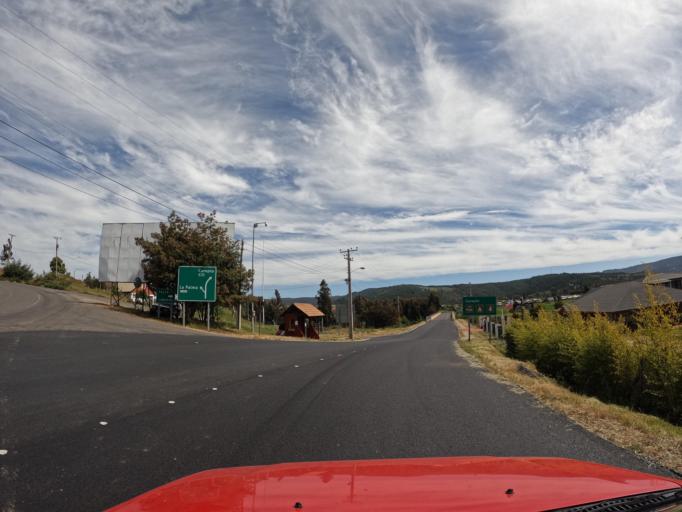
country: CL
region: Maule
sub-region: Provincia de Talca
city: Constitucion
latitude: -35.0849
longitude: -72.0172
